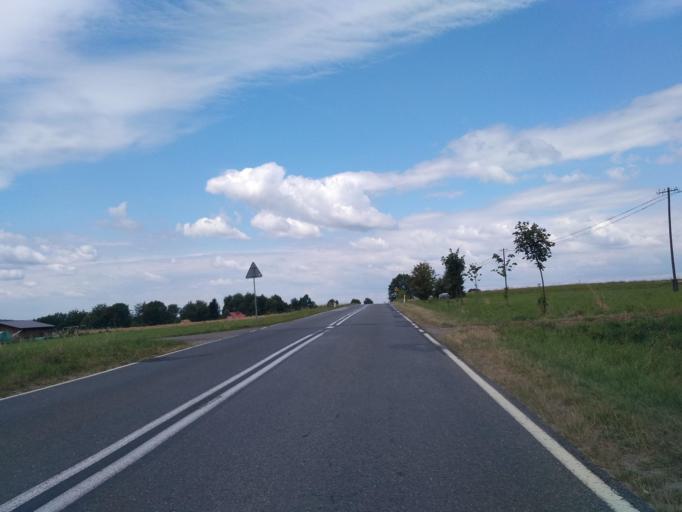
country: PL
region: Subcarpathian Voivodeship
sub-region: Powiat rzeszowski
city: Hyzne
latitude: 49.8945
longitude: 22.2297
